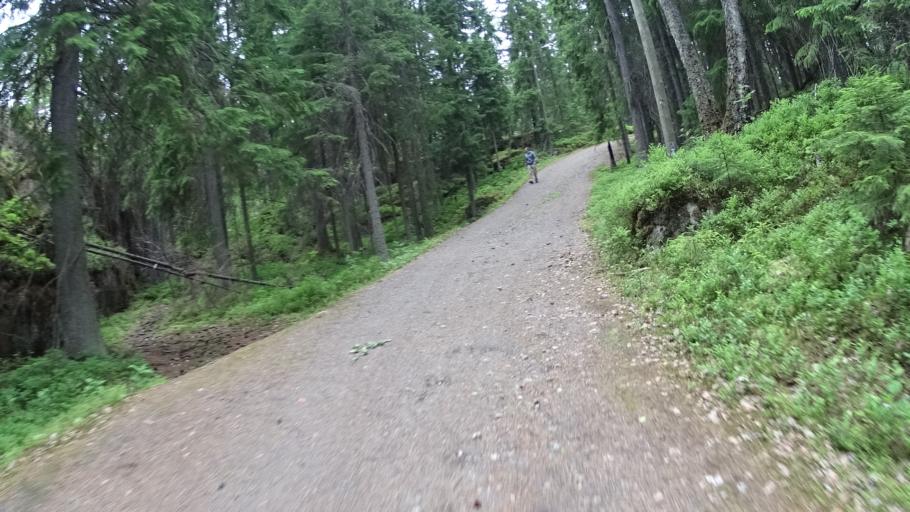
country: FI
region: Uusimaa
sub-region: Helsinki
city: Espoo
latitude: 60.2942
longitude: 24.5714
